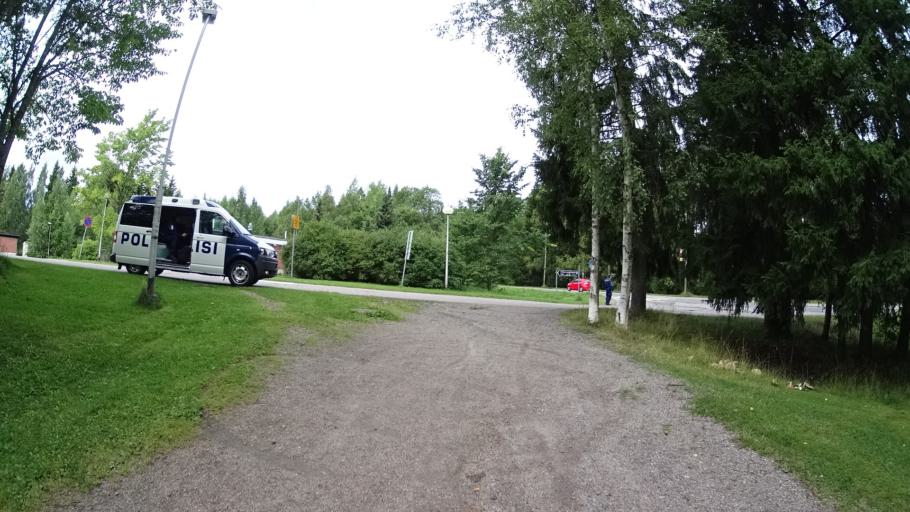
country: FI
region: Uusimaa
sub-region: Helsinki
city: Teekkarikylae
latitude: 60.2676
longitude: 24.8607
